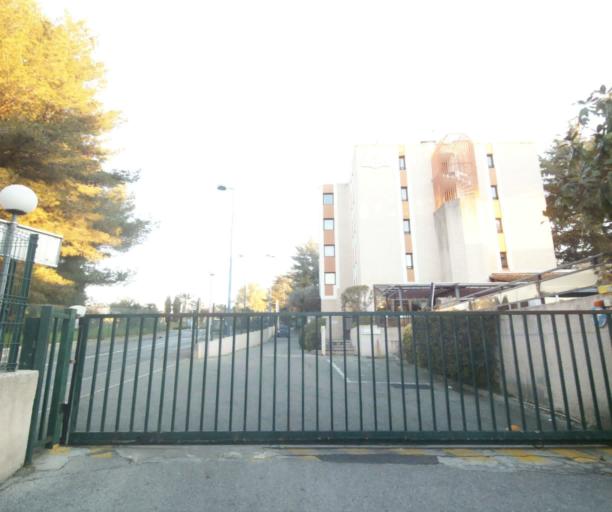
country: FR
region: Provence-Alpes-Cote d'Azur
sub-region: Departement des Alpes-Maritimes
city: Biot
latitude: 43.6015
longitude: 7.0917
